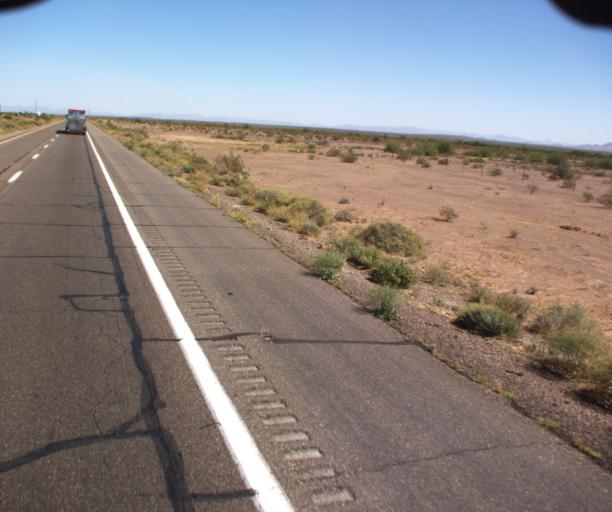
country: US
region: Arizona
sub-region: Maricopa County
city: Gila Bend
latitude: 32.8965
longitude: -113.0254
